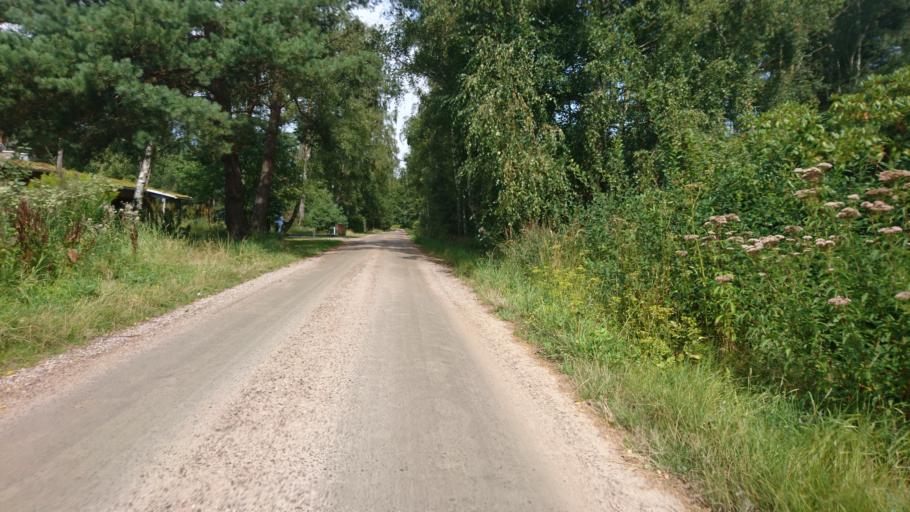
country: SE
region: Skane
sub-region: Vellinge Kommun
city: Ljunghusen
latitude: 55.4034
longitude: 12.9099
